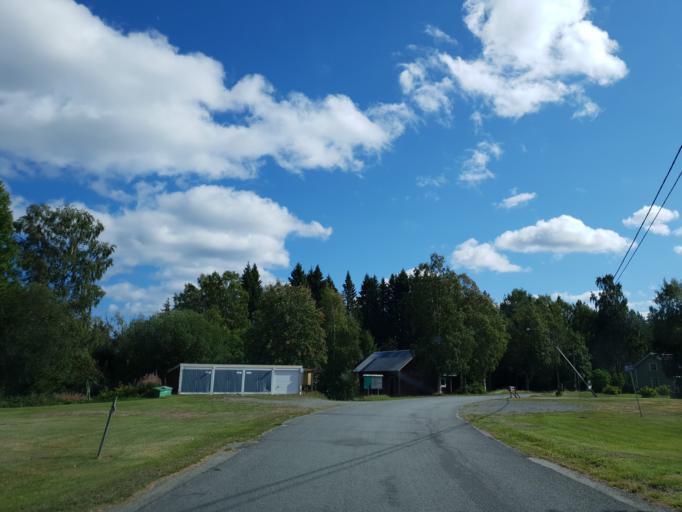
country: SE
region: Vaesternorrland
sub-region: OErnskoeldsviks Kommun
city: Husum
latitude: 63.3401
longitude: 19.1155
